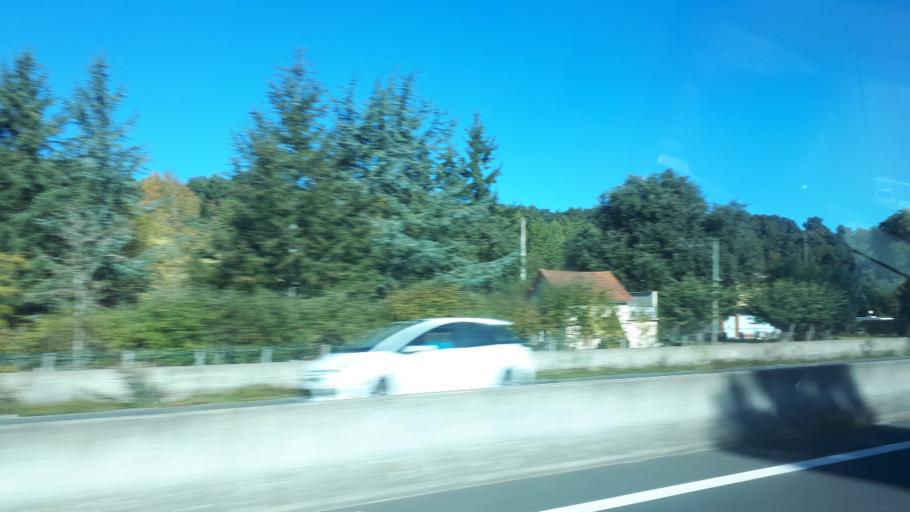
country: FR
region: Centre
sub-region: Departement du Loir-et-Cher
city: Moree
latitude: 47.8820
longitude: 1.1652
